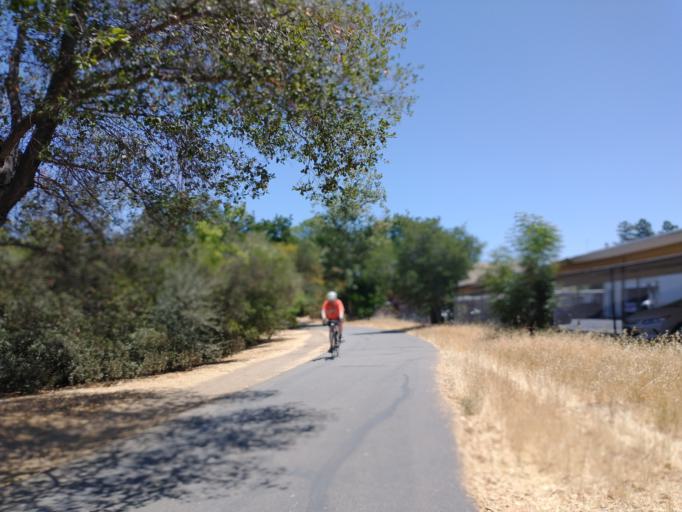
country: US
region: California
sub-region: Santa Clara County
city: Campbell
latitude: 37.2973
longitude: -121.9301
